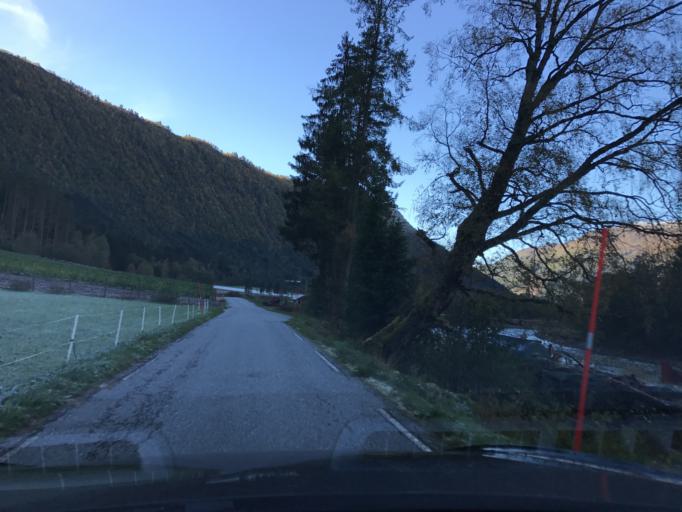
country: NO
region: More og Romsdal
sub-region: Norddal
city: Valldal
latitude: 62.3208
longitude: 7.3257
